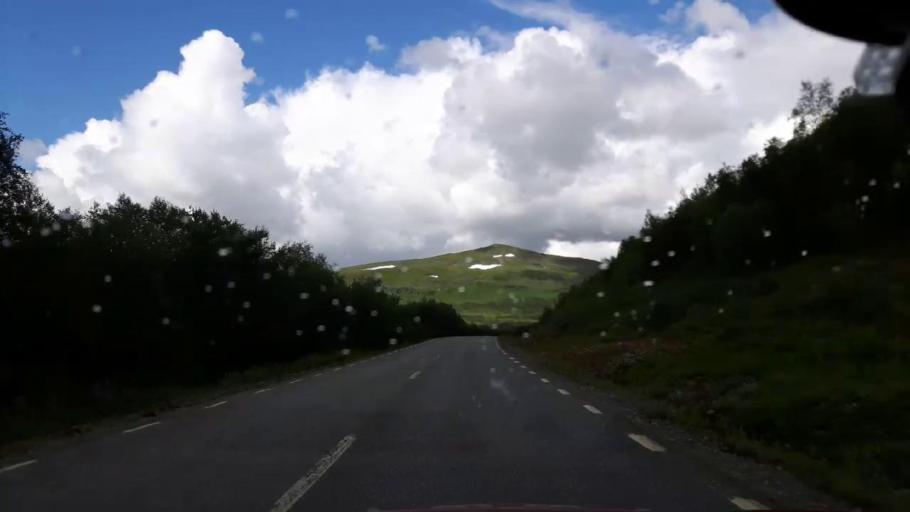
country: NO
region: Nordland
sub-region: Hattfjelldal
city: Hattfjelldal
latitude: 65.0690
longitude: 14.6652
